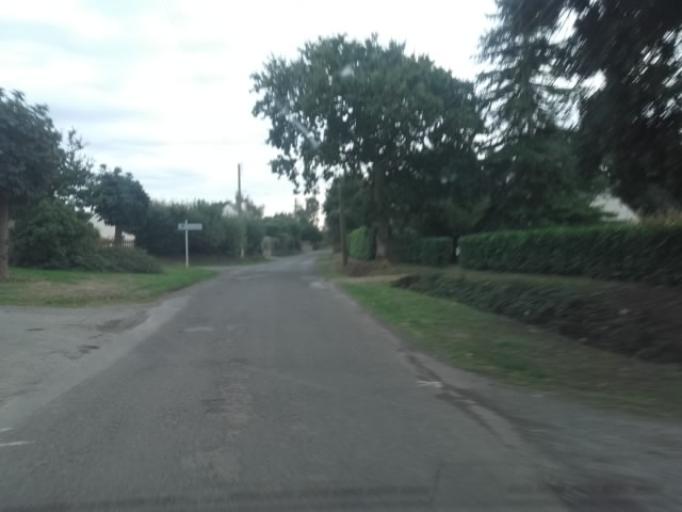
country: FR
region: Brittany
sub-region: Departement des Cotes-d'Armor
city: Pleguien
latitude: 48.6397
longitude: -2.9396
